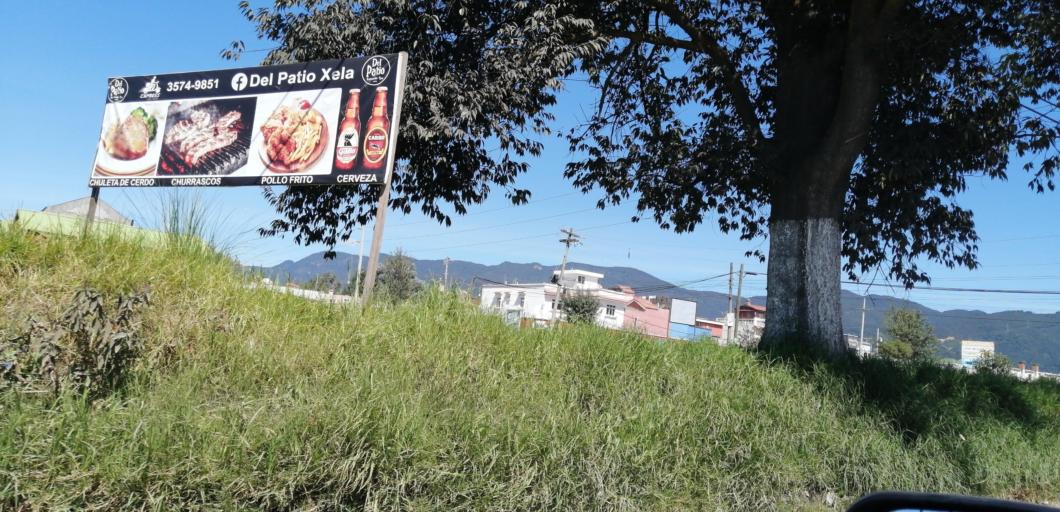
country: GT
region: Quetzaltenango
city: Olintepeque
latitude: 14.8668
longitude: -91.5258
